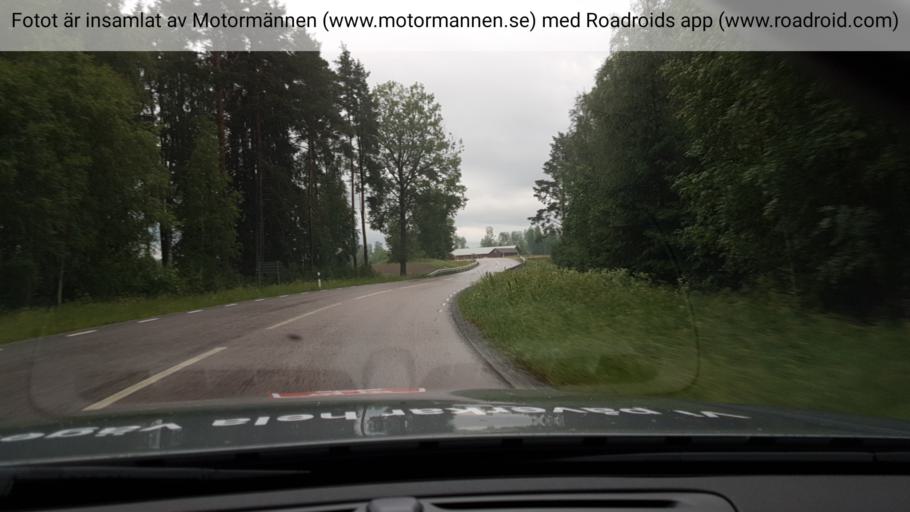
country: SE
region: Vaestmanland
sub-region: Sala Kommun
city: Sala
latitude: 59.9182
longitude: 16.4573
